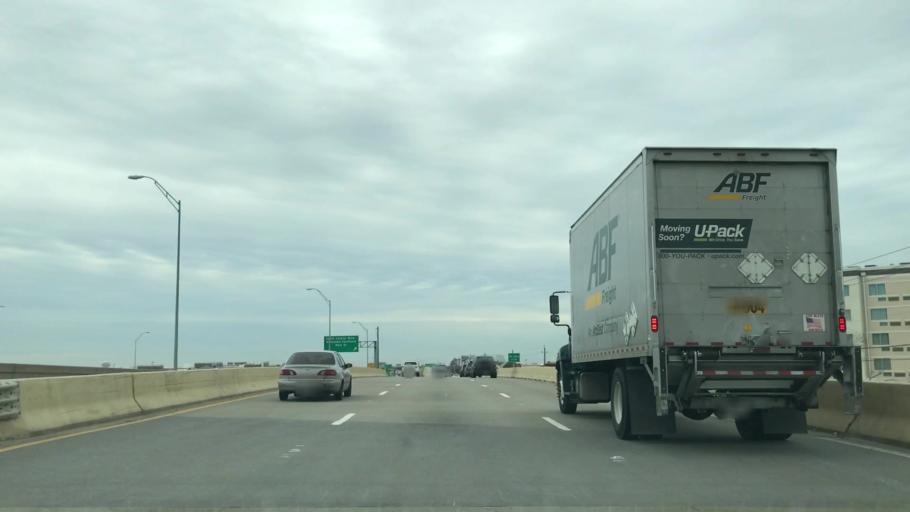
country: US
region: Texas
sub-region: Denton County
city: The Colony
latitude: 33.0817
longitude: -96.8553
